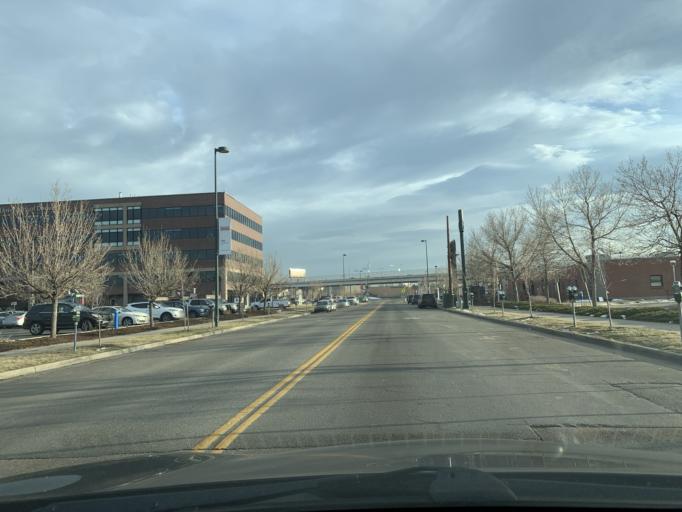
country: US
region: Colorado
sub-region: Denver County
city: Denver
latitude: 39.7423
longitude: -105.0105
